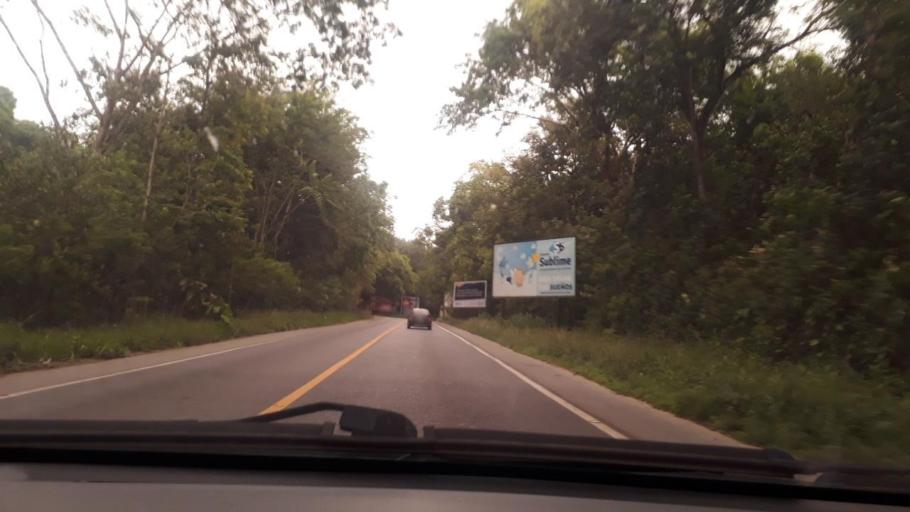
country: GT
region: Izabal
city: Morales
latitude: 15.5013
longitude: -88.8501
